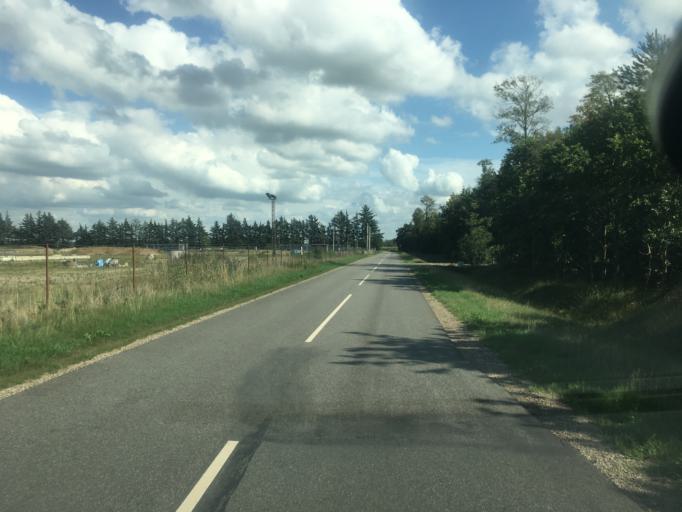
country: DE
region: Schleswig-Holstein
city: Ellhoft
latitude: 54.9666
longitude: 8.9739
